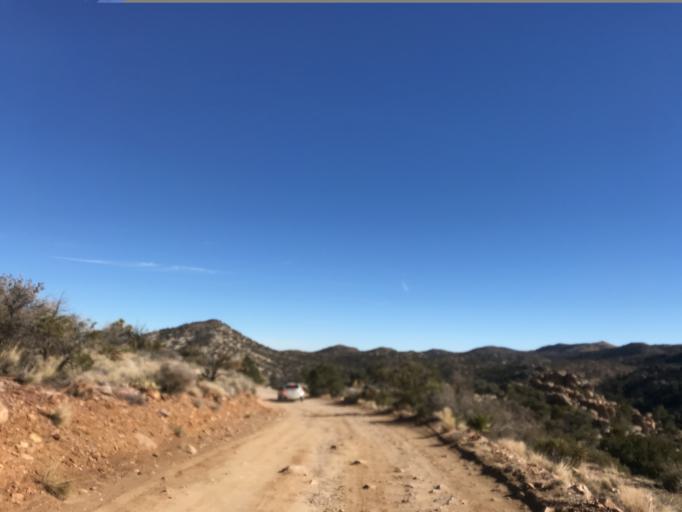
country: US
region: California
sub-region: San Bernardino County
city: Big Bear City
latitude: 34.2274
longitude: -116.6724
